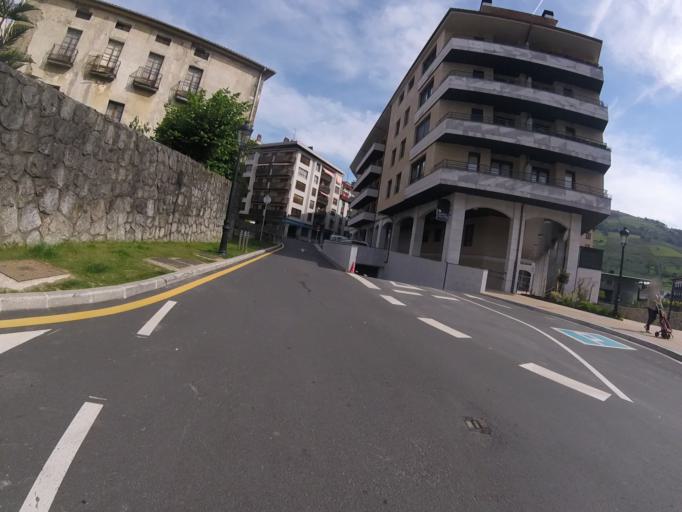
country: ES
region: Basque Country
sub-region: Provincia de Guipuzcoa
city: Azpeitia
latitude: 43.1829
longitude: -2.2668
